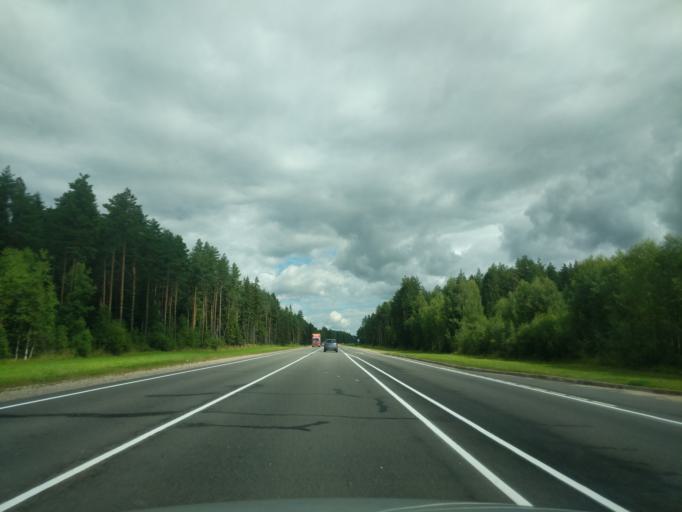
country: RU
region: Jaroslavl
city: Nekrasovskoye
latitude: 57.5951
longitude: 40.3071
